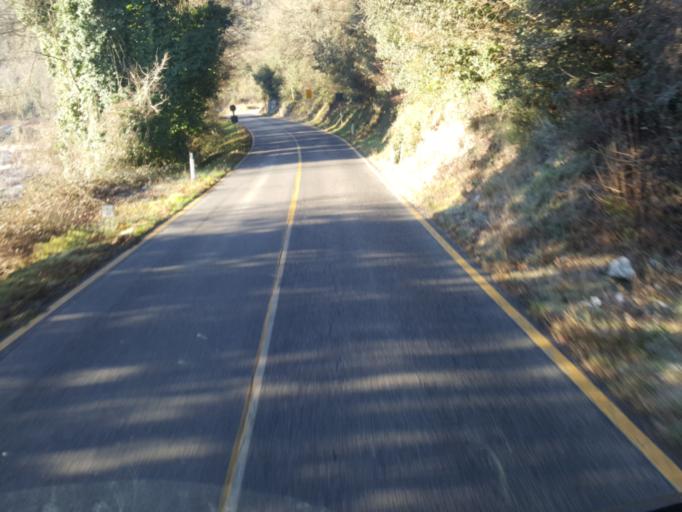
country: IT
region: Umbria
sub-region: Provincia di Terni
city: Arrone
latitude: 42.5335
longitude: 12.7312
